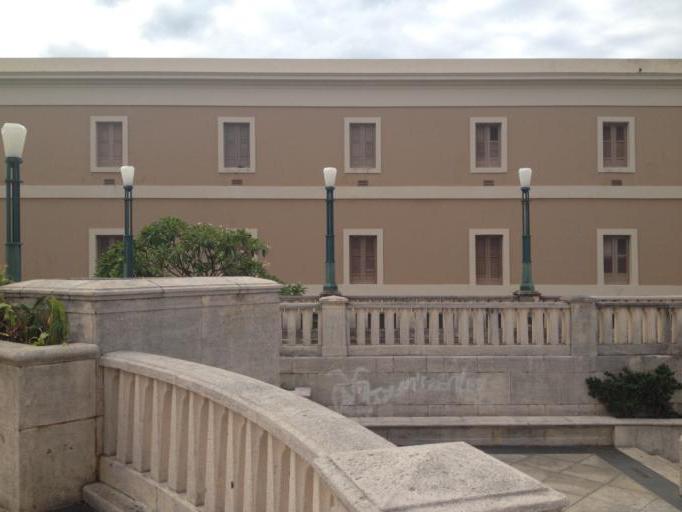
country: PR
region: San Juan
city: San Juan
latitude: 18.4679
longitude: -66.1190
